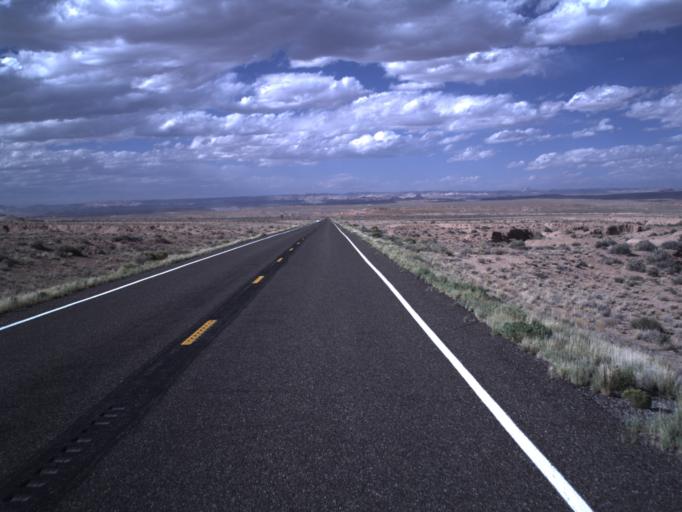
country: US
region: Utah
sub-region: Emery County
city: Ferron
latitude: 38.2759
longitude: -110.6609
